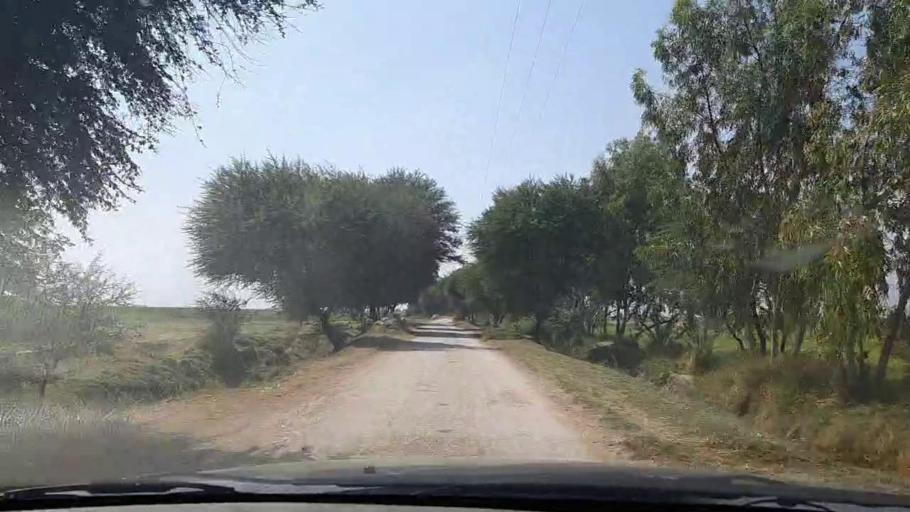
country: PK
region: Sindh
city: Mirpur Batoro
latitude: 24.6107
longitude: 68.2384
